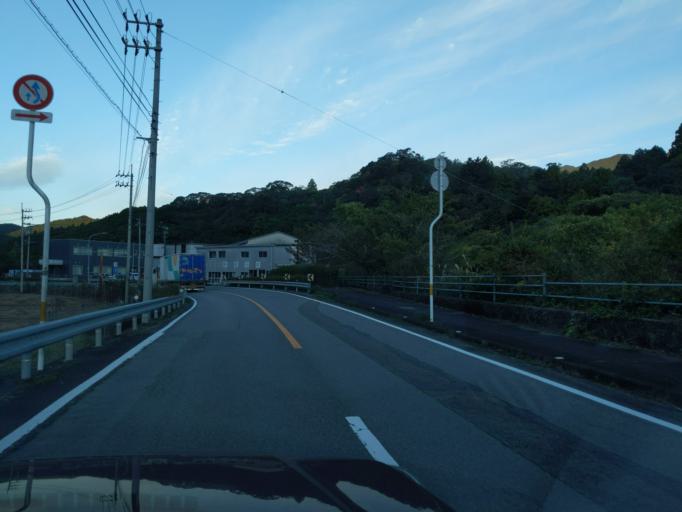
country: JP
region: Tokushima
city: Anan
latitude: 33.6899
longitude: 134.4284
